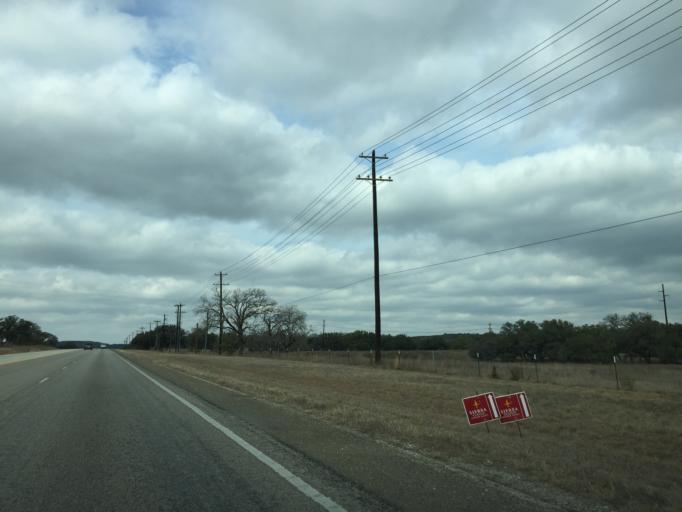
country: US
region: Texas
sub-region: Travis County
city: Briarcliff
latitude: 30.4139
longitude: -98.1160
